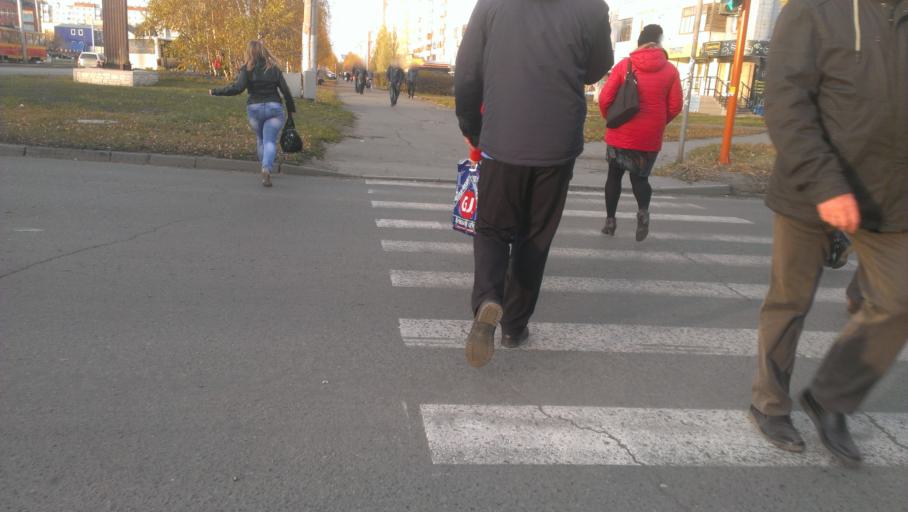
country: RU
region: Altai Krai
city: Novosilikatnyy
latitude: 53.3360
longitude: 83.6695
